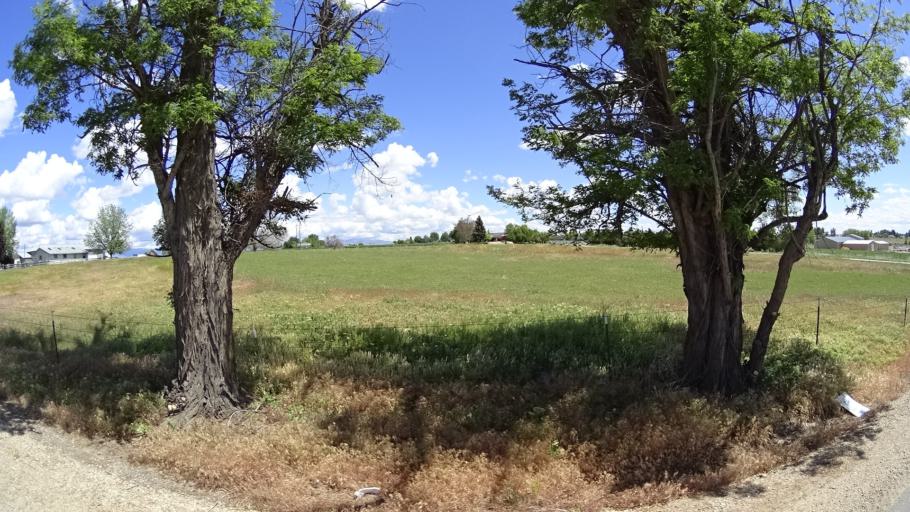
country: US
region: Idaho
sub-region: Ada County
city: Kuna
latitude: 43.5564
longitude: -116.4337
